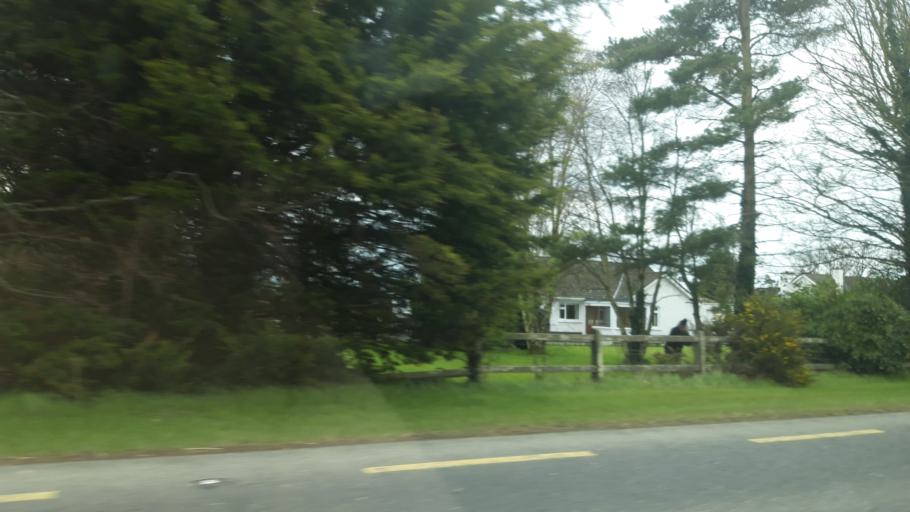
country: IE
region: Leinster
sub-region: Kildare
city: Clane
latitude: 53.3127
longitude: -6.6512
